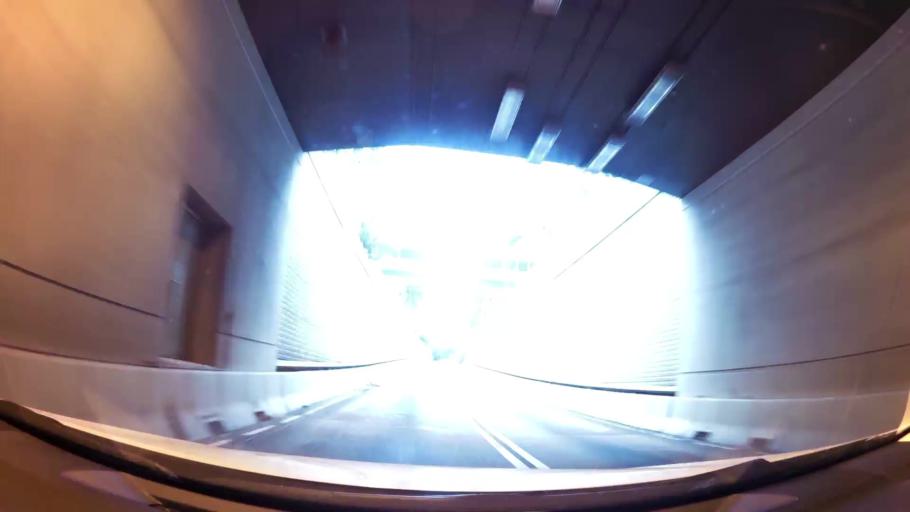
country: HK
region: Kowloon City
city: Kowloon
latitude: 22.3038
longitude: 114.1872
